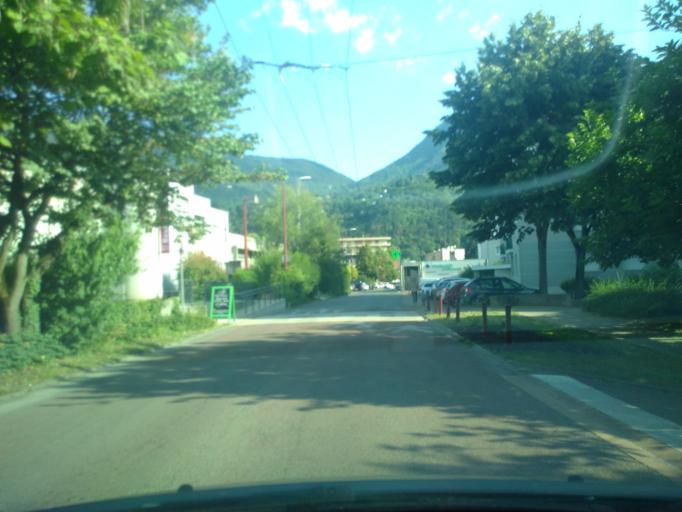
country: FR
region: Rhone-Alpes
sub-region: Departement de l'Isere
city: Corenc
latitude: 45.2069
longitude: 5.7638
